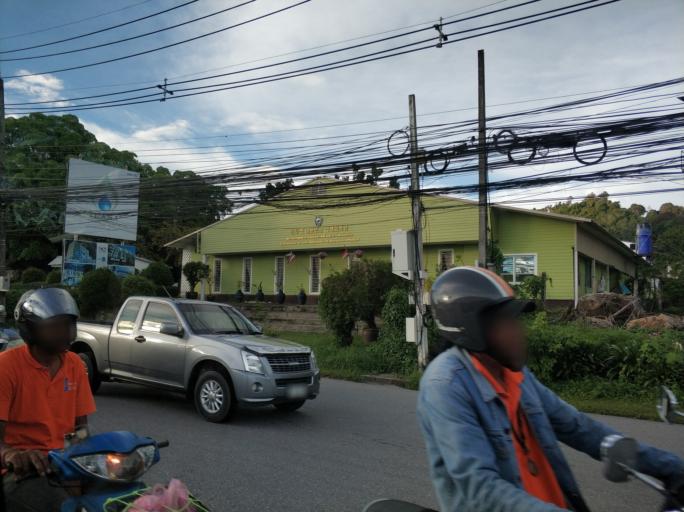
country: TH
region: Phuket
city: Wichit
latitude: 7.8884
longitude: 98.3705
